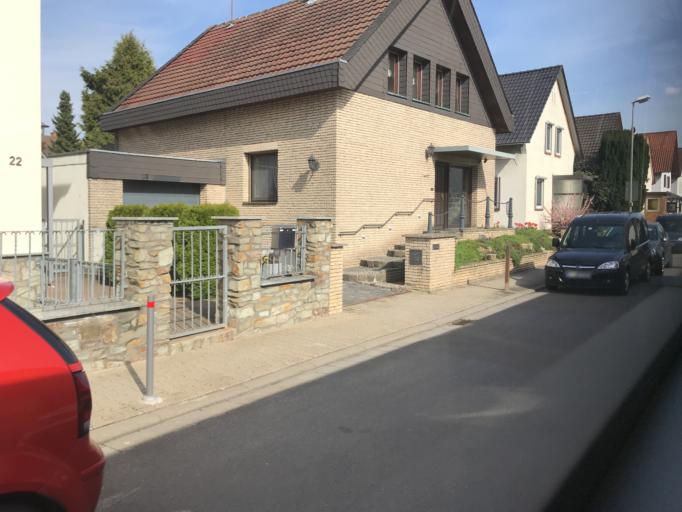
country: DE
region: Hesse
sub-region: Regierungsbezirk Darmstadt
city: Ginsheim-Gustavsburg
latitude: 49.9620
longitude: 8.3208
